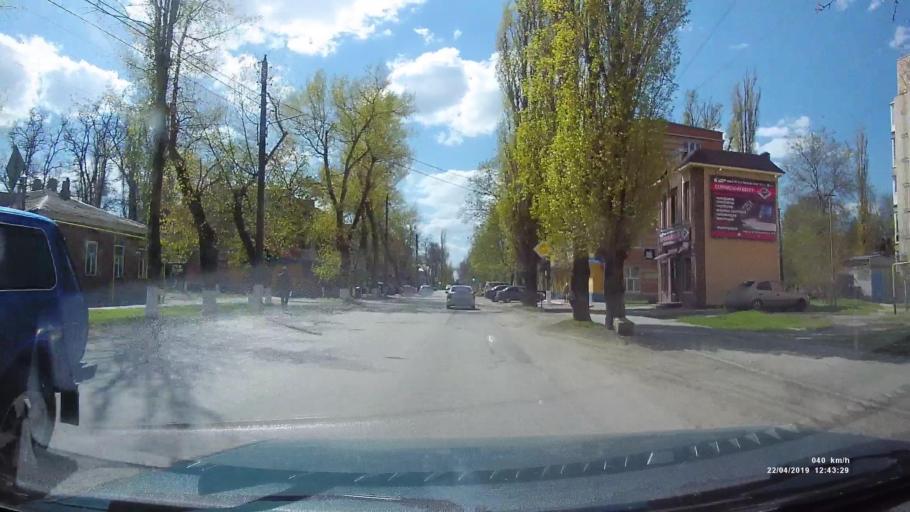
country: RU
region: Rostov
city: Azov
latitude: 47.1025
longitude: 39.4231
